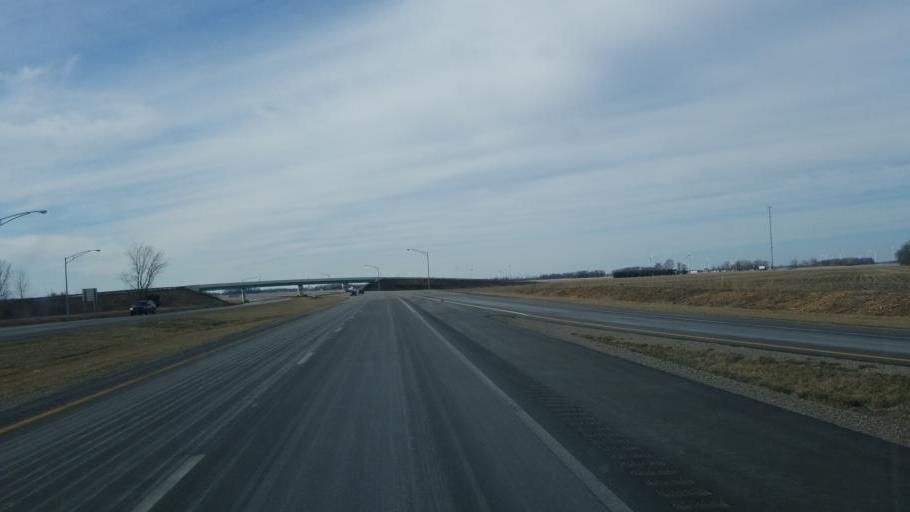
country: US
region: Ohio
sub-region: Van Wert County
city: Van Wert
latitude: 40.8808
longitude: -84.5261
